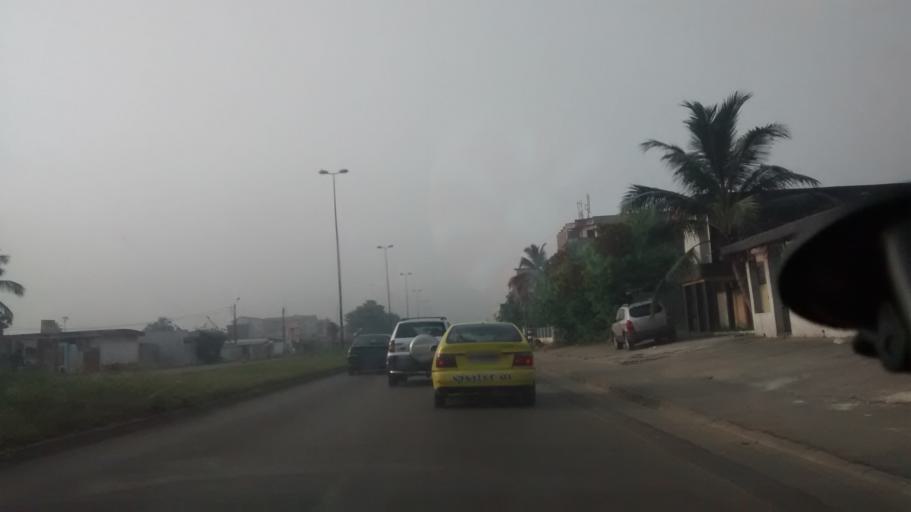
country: CI
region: Lagunes
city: Abobo
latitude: 5.4026
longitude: -3.9910
